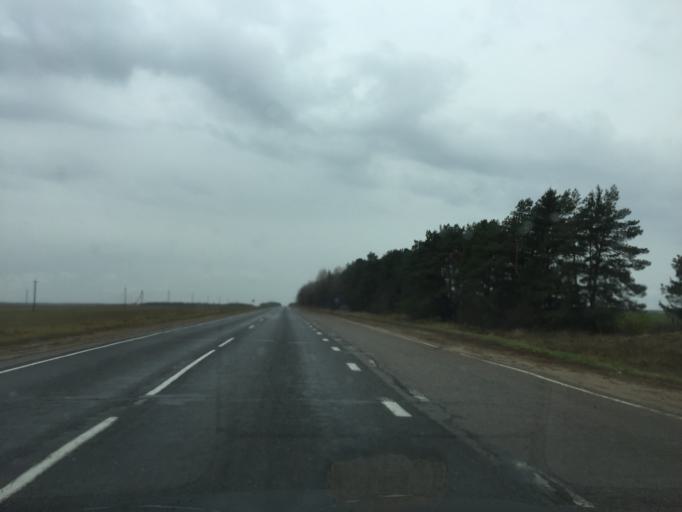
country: BY
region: Mogilev
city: Slawharad
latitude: 53.3947
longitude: 30.9101
